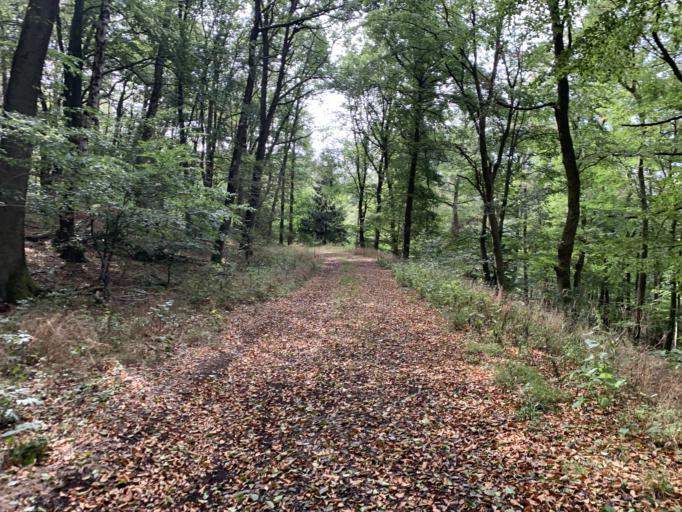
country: DE
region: Rheinland-Pfalz
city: Rettert
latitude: 50.2233
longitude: 7.9389
